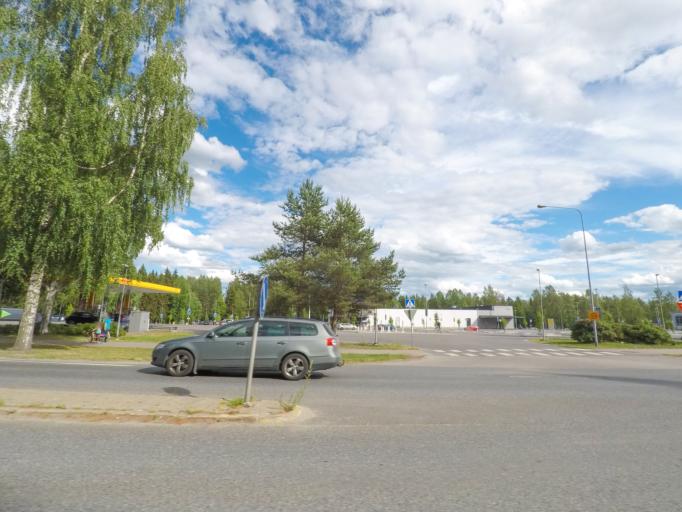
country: FI
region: Paijanne Tavastia
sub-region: Lahti
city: Lahti
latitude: 60.9696
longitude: 25.6291
